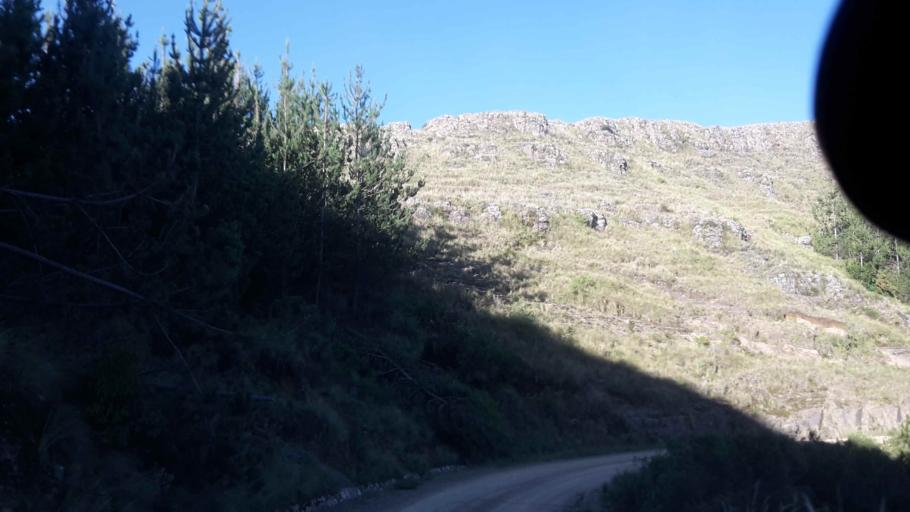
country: BO
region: Cochabamba
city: Arani
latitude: -17.7306
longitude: -65.6262
